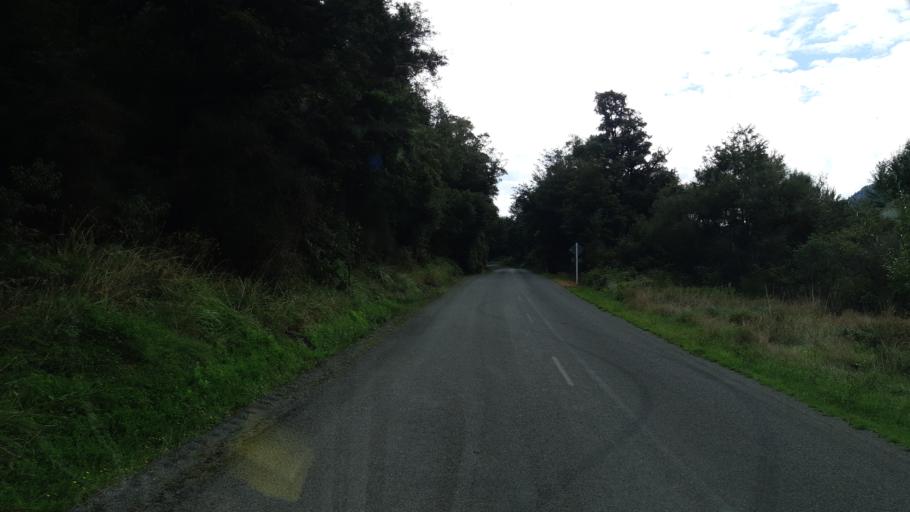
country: NZ
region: West Coast
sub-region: Buller District
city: Westport
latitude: -41.7772
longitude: 172.3723
